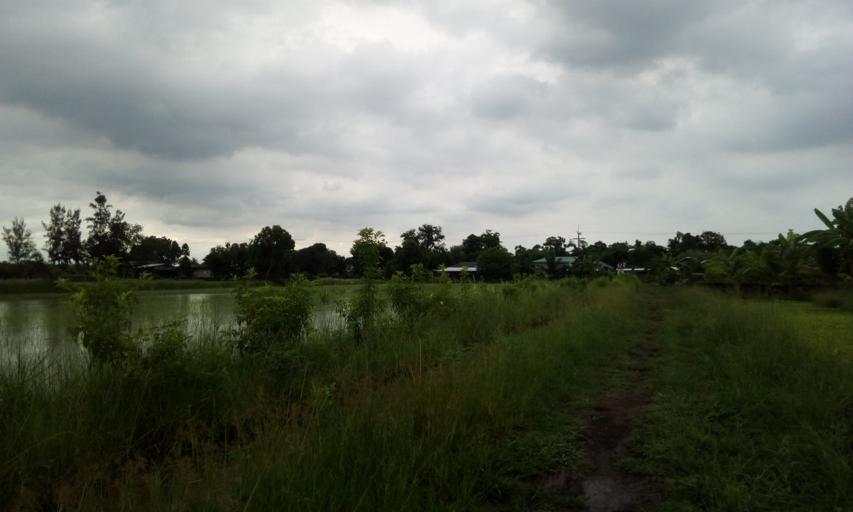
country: TH
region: Nakhon Nayok
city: Ongkharak
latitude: 14.0896
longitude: 100.9129
